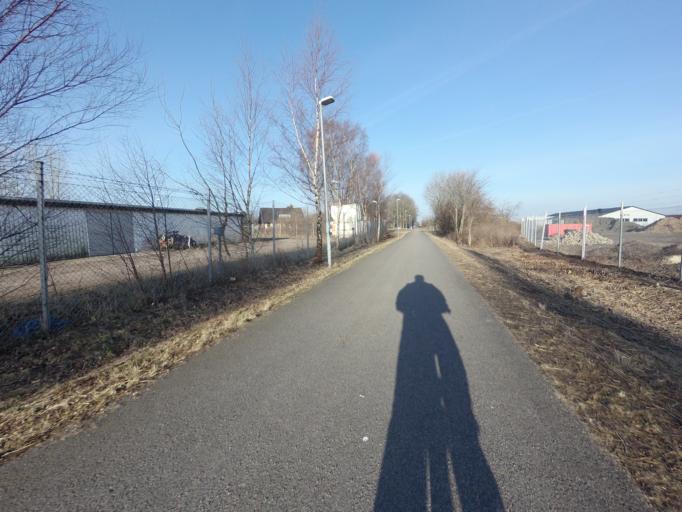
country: SE
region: Skane
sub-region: Hoganas Kommun
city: Hoganas
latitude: 56.2003
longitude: 12.5840
